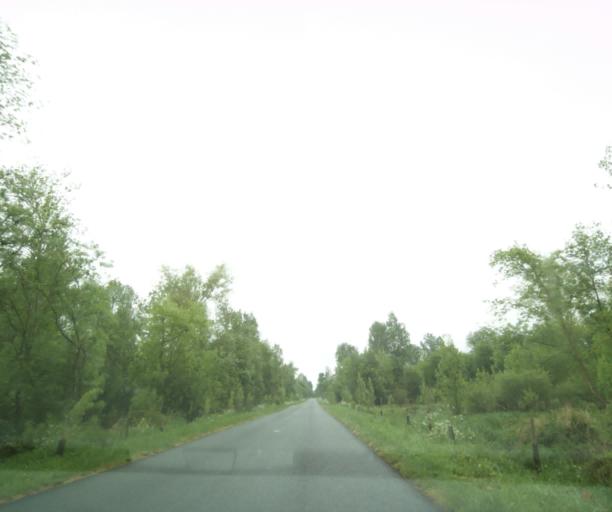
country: FR
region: Poitou-Charentes
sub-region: Departement de la Charente-Maritime
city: Pons
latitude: 45.6464
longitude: -0.5449
